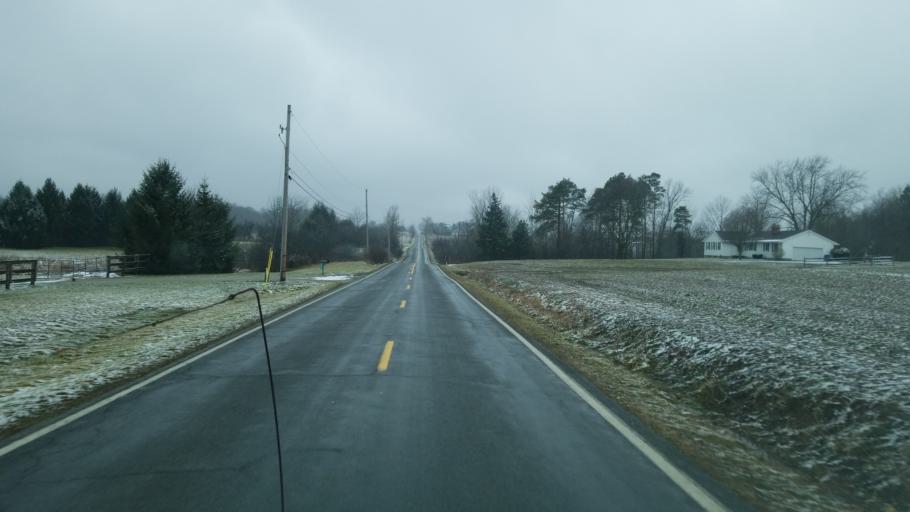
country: US
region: Ohio
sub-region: Portage County
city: Mantua
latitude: 41.2841
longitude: -81.2769
